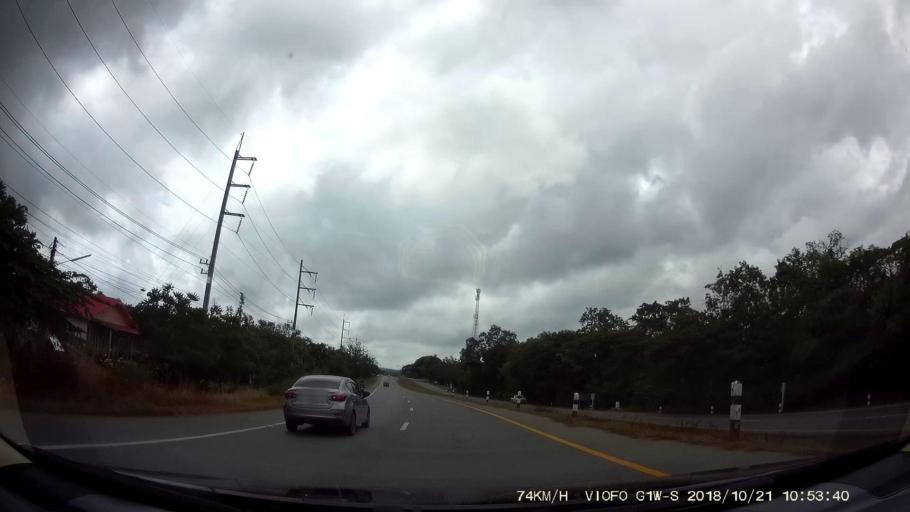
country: TH
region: Chaiyaphum
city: Khon Sawan
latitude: 15.9624
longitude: 102.1804
